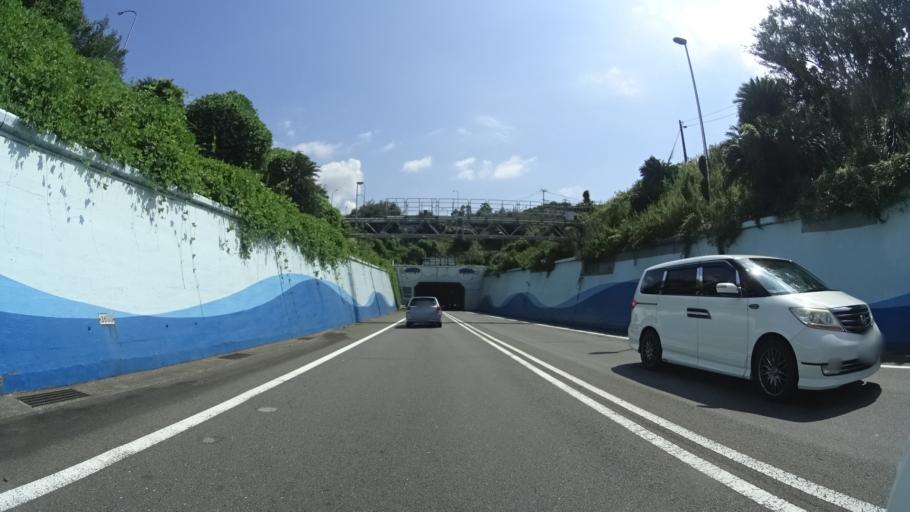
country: JP
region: Yamaguchi
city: Shimonoseki
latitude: 33.9758
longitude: 130.9471
